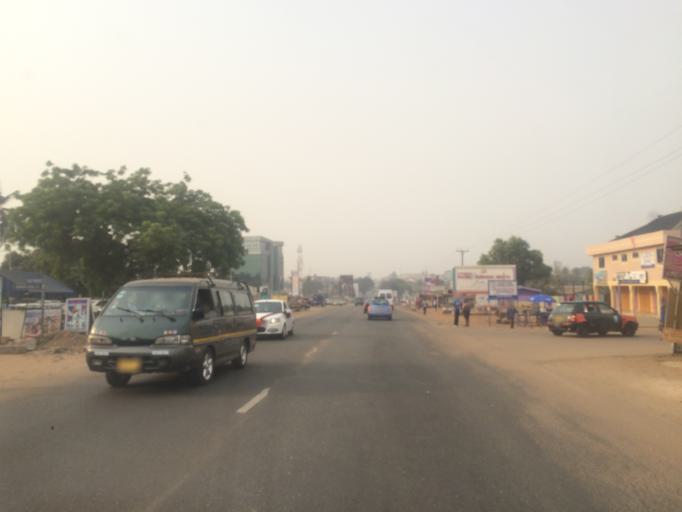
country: GH
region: Greater Accra
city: Nungua
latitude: 5.6107
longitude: -0.0755
